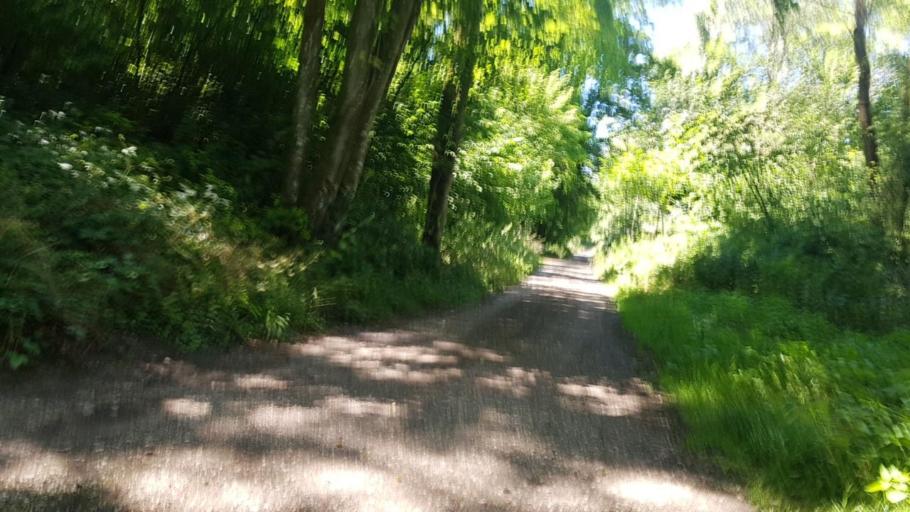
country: FR
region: Ile-de-France
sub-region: Departement de Seine-et-Marne
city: Nanteuil-les-Meaux
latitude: 48.9360
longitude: 2.8916
